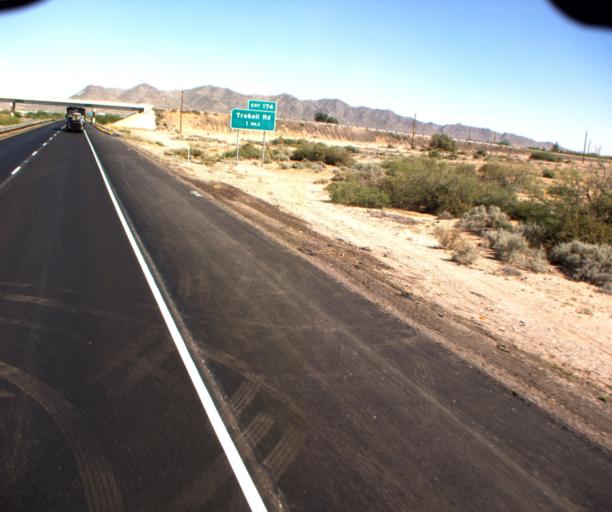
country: US
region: Arizona
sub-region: Pinal County
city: Casa Grande
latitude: 32.8279
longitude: -111.7596
